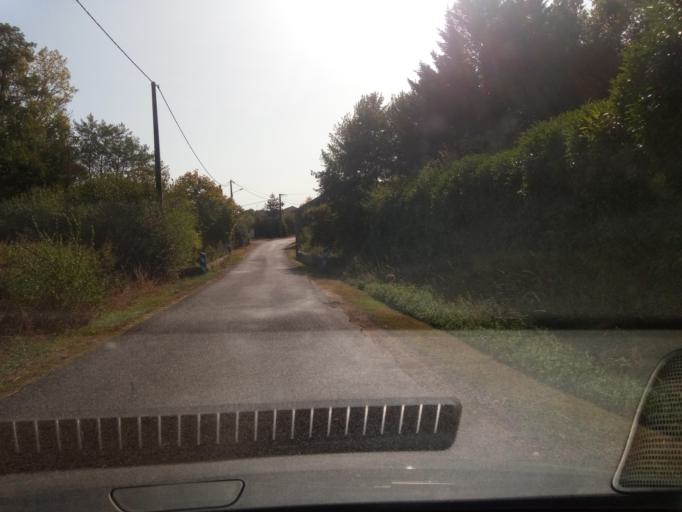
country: FR
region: Poitou-Charentes
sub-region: Departement de la Vienne
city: Saulge
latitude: 46.3309
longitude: 0.8332
